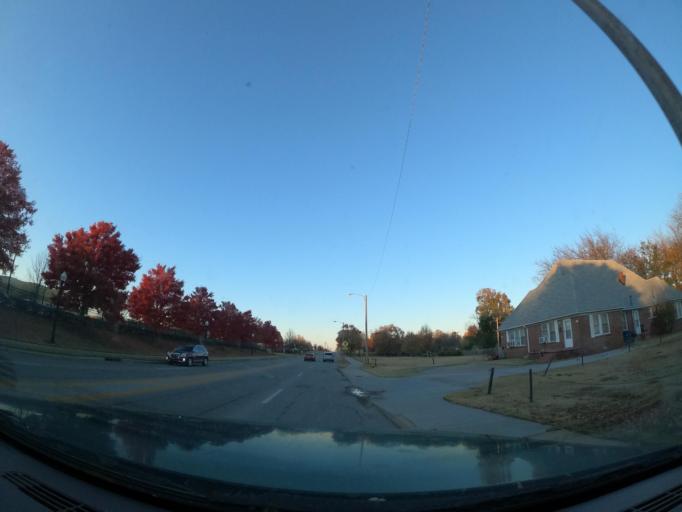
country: US
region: Oklahoma
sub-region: Tulsa County
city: Tulsa
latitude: 36.1488
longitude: -95.9403
